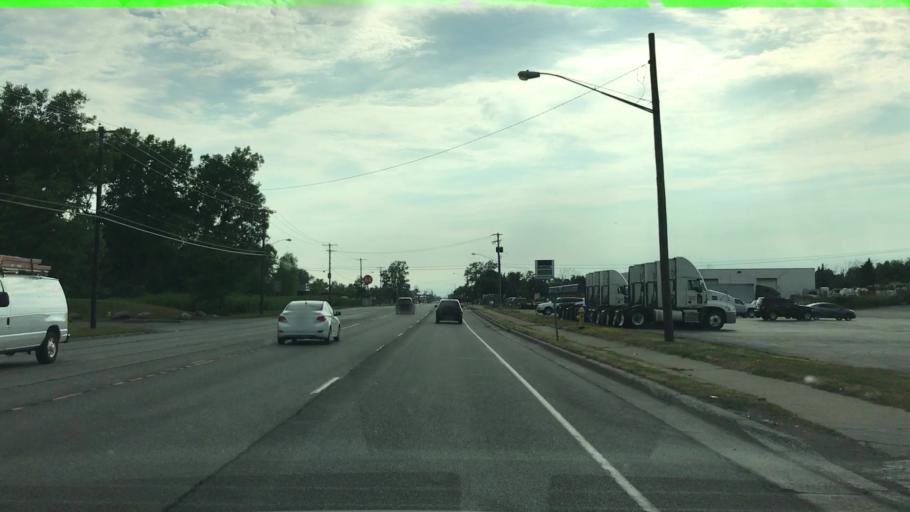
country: US
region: New York
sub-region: Erie County
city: Depew
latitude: 42.9136
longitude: -78.6868
